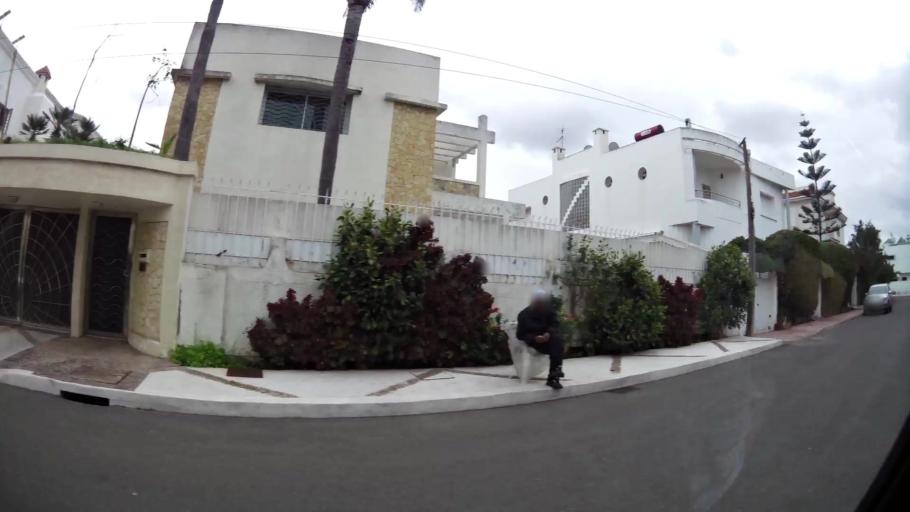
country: MA
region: Grand Casablanca
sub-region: Casablanca
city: Casablanca
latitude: 33.5996
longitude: -7.6533
